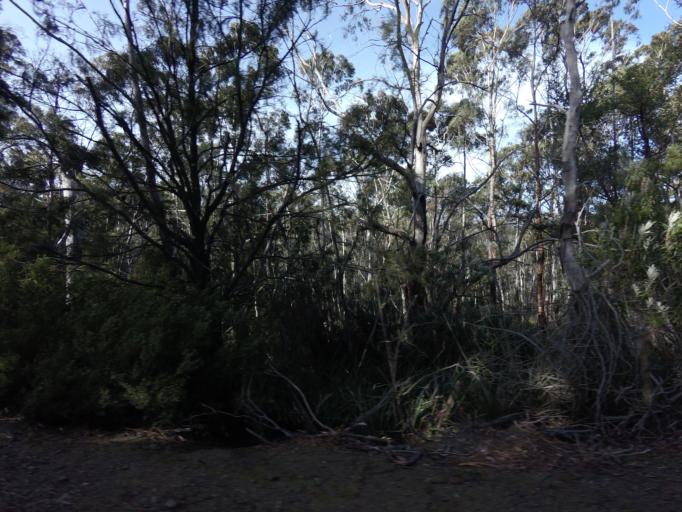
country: AU
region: Tasmania
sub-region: Kingborough
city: Kettering
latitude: -43.1046
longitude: 147.2602
